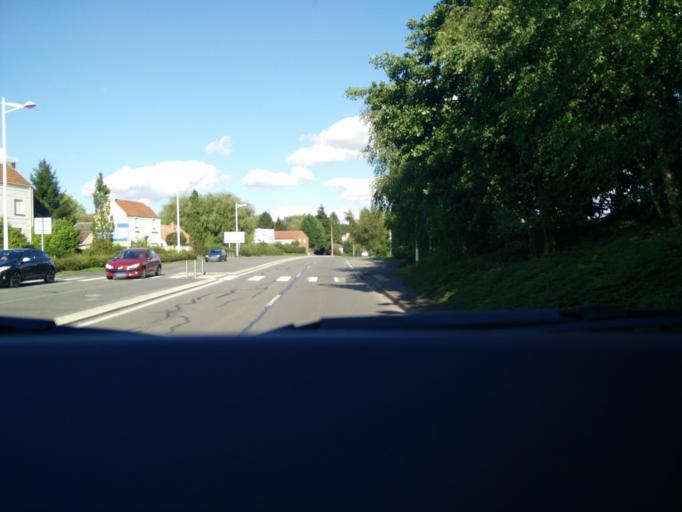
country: FR
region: Nord-Pas-de-Calais
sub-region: Departement du Nord
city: Feignies
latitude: 50.2802
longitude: 3.9245
